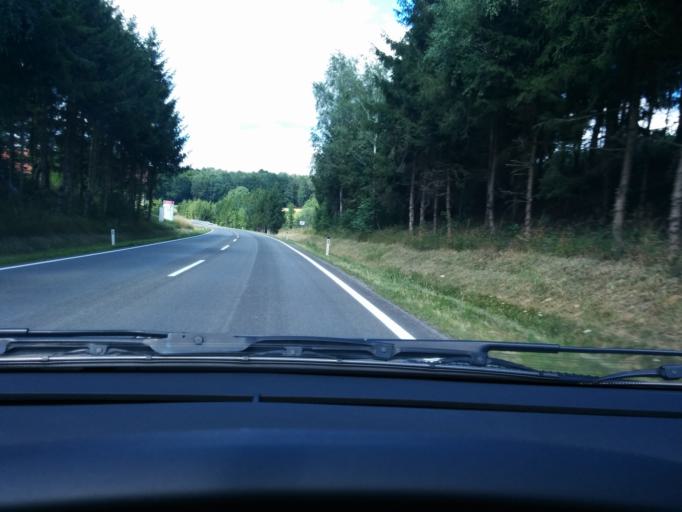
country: AT
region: Styria
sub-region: Politischer Bezirk Hartberg-Fuerstenfeld
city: Hartberg
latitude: 47.3032
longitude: 15.9830
